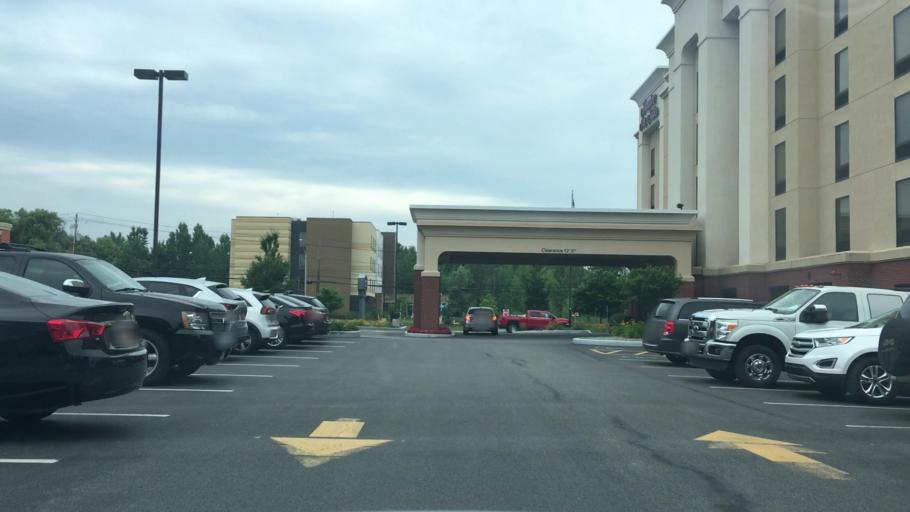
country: US
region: New York
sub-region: Clinton County
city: Plattsburgh West
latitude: 44.6967
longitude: -73.5048
